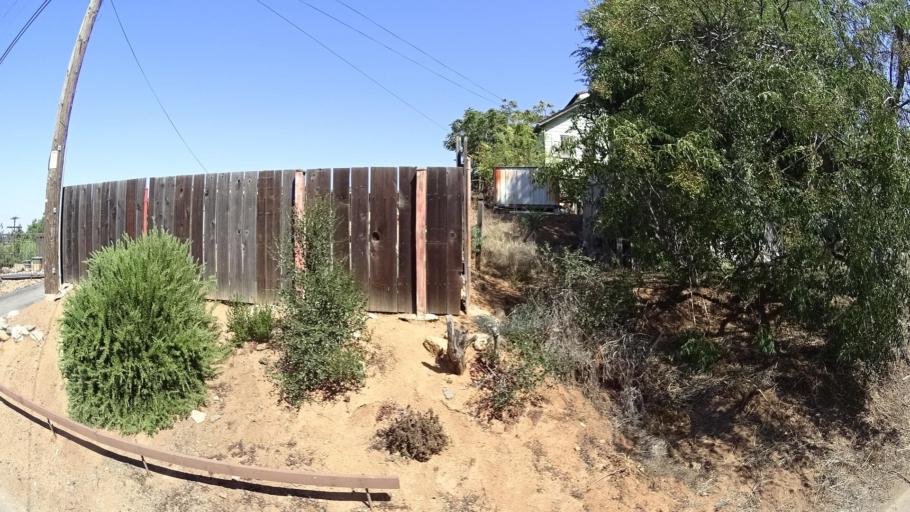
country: US
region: California
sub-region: San Diego County
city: Crest
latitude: 32.8094
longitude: -116.8678
